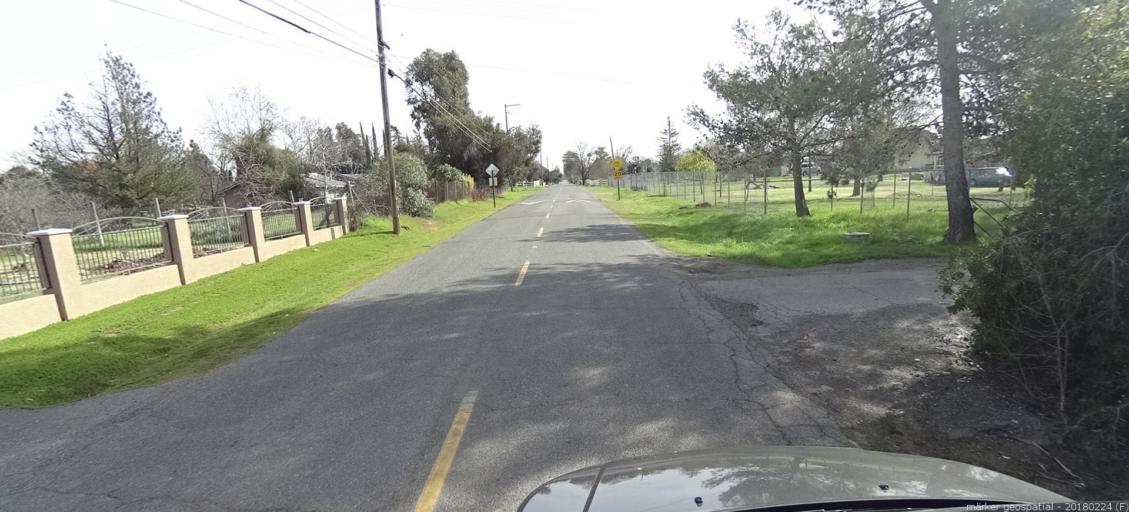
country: US
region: California
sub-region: Sacramento County
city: Rio Linda
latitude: 38.6800
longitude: -121.4341
